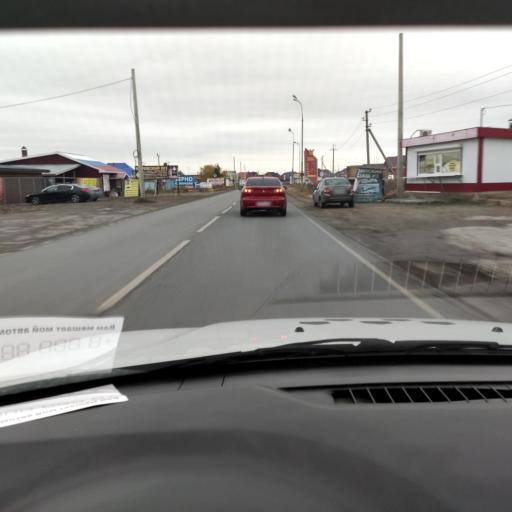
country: RU
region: Samara
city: Podstepki
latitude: 53.5177
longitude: 49.2193
